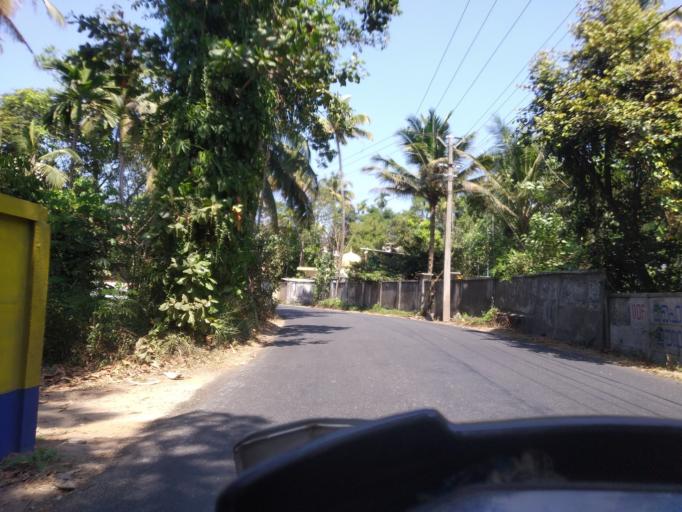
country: IN
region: Kerala
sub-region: Thrissur District
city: Kodungallur
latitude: 10.1625
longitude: 76.2144
